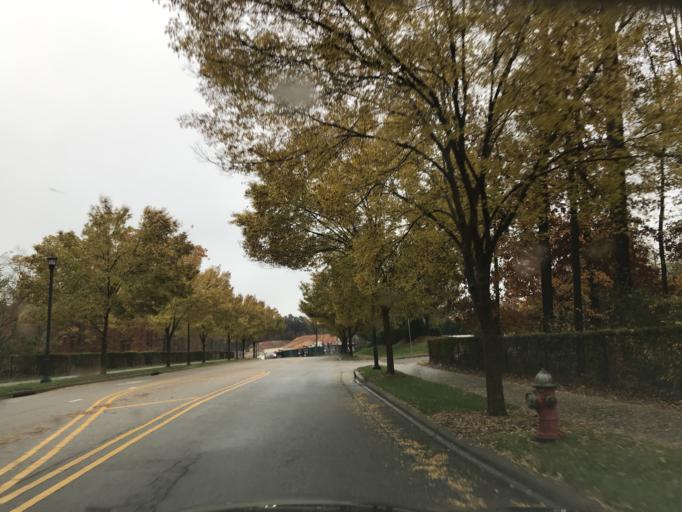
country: US
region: North Carolina
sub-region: Wake County
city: West Raleigh
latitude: 35.8361
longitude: -78.6334
